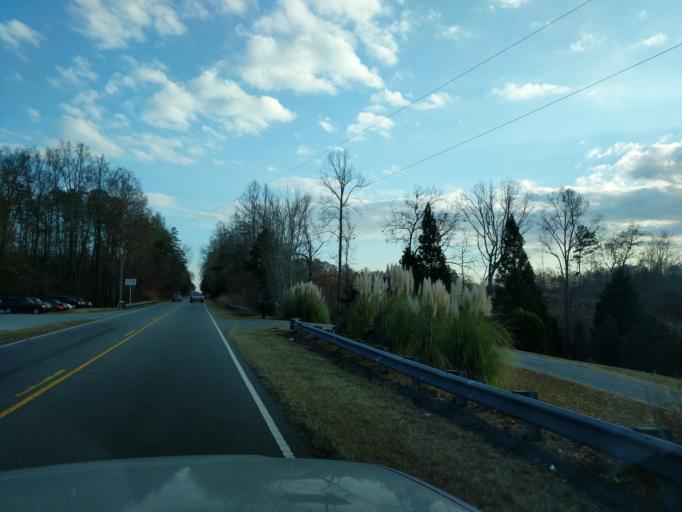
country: US
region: North Carolina
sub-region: Rutherford County
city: Rutherfordton
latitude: 35.4198
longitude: -81.9765
